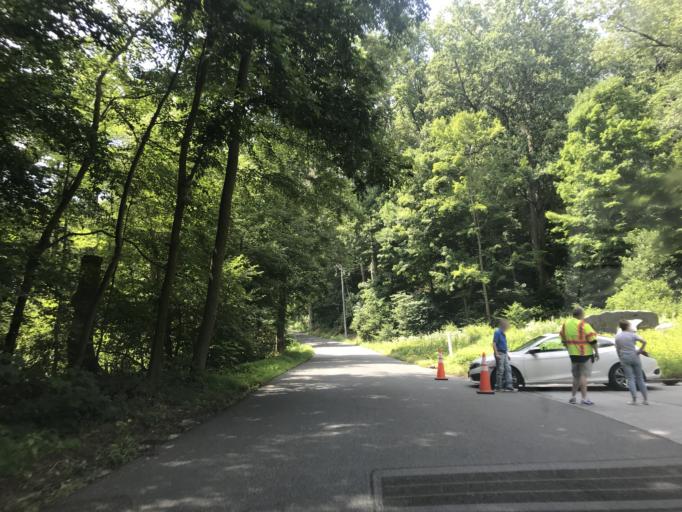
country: US
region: Delaware
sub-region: New Castle County
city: Hockessin
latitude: 39.7855
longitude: -75.6503
